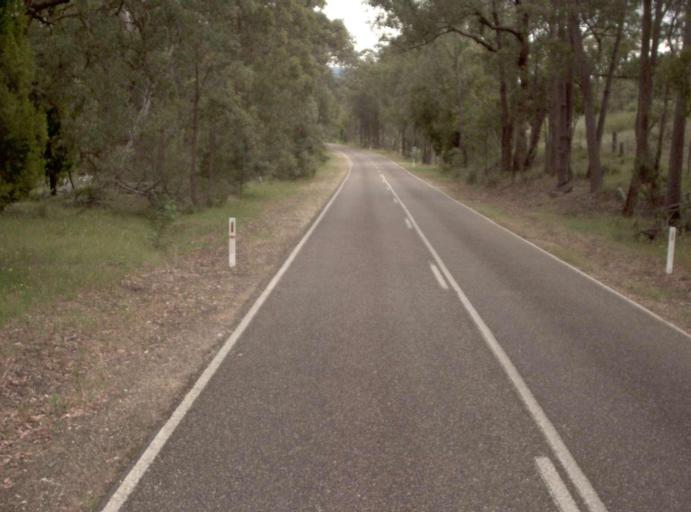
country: AU
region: Victoria
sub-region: East Gippsland
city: Bairnsdale
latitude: -37.7846
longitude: 147.3242
